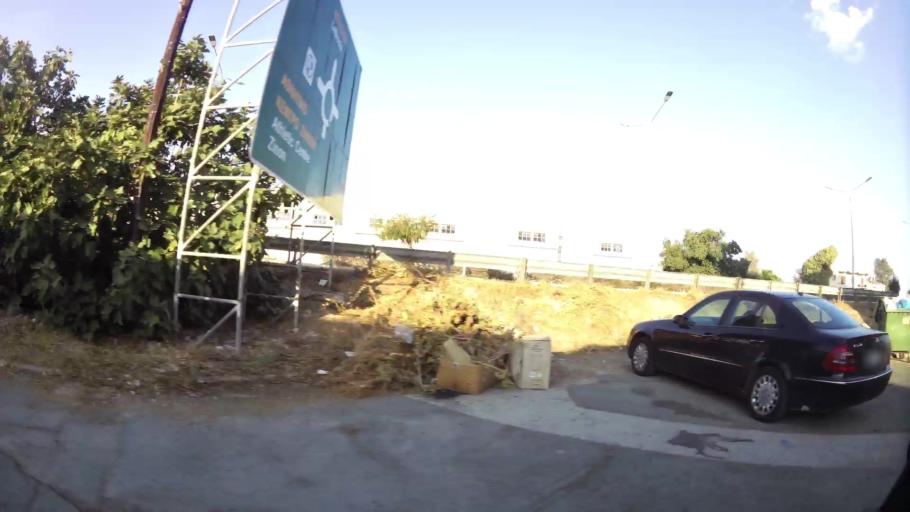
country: CY
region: Larnaka
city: Larnaca
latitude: 34.9263
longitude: 33.6067
